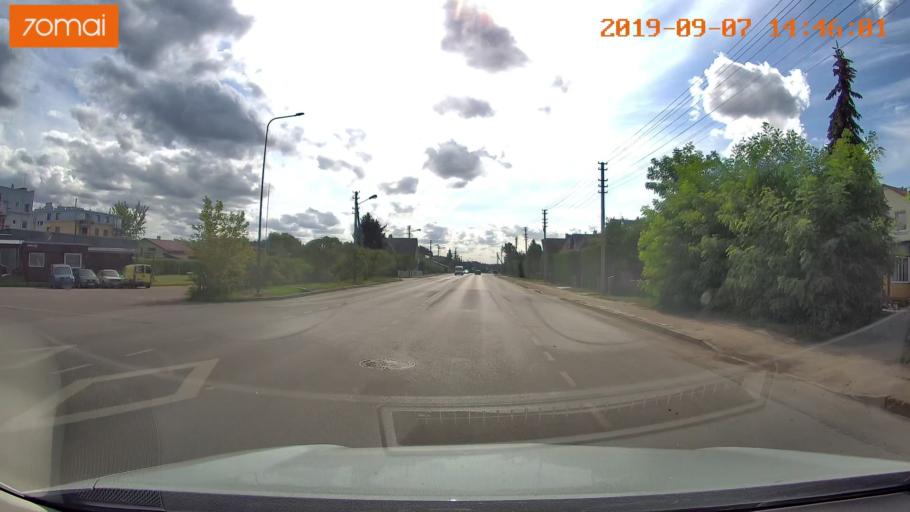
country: LT
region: Kauno apskritis
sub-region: Kaunas
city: Silainiai
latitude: 54.9289
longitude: 23.9070
